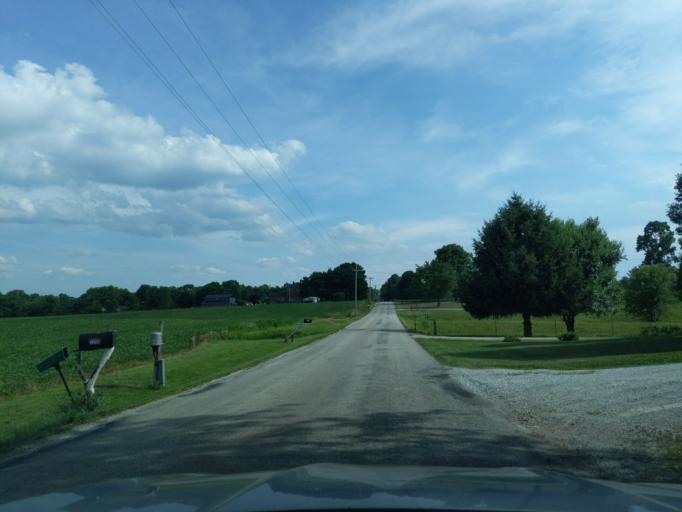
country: US
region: Indiana
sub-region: Decatur County
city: Greensburg
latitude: 39.3034
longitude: -85.4702
